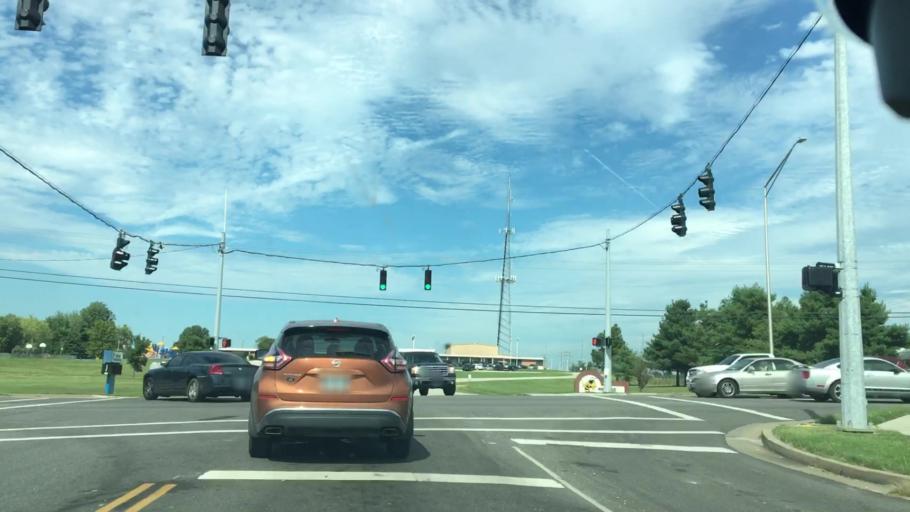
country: US
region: Kentucky
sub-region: Daviess County
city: Owensboro
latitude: 37.7560
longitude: -87.0673
